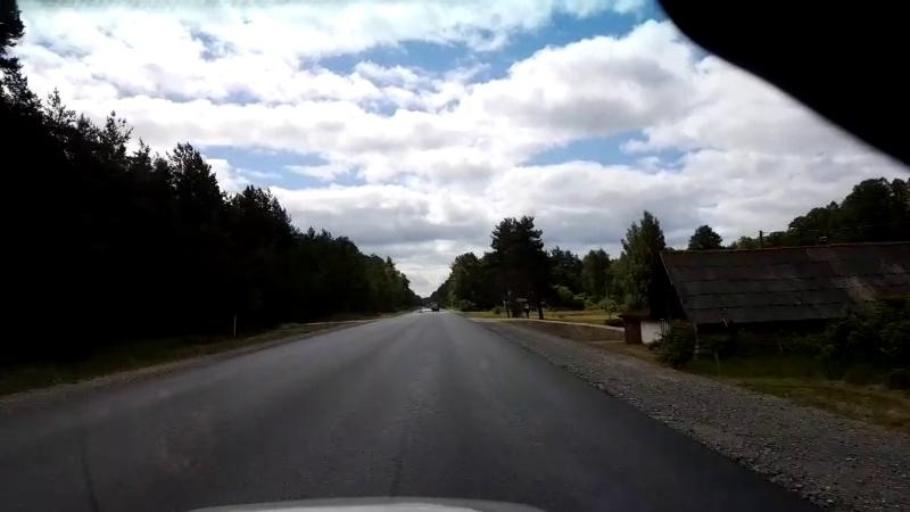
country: LV
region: Salacgrivas
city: Salacgriva
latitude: 57.8074
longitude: 24.3484
